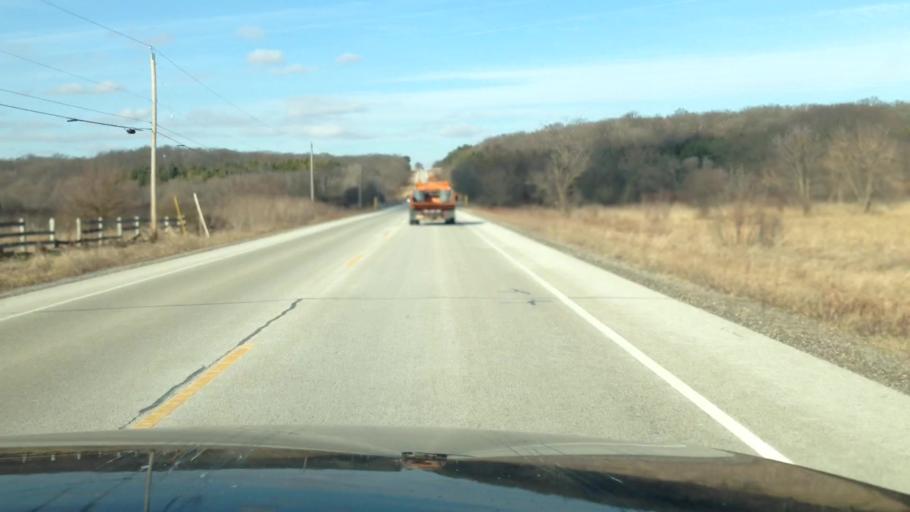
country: US
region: Wisconsin
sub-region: Walworth County
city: East Troy
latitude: 42.7292
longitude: -88.4057
